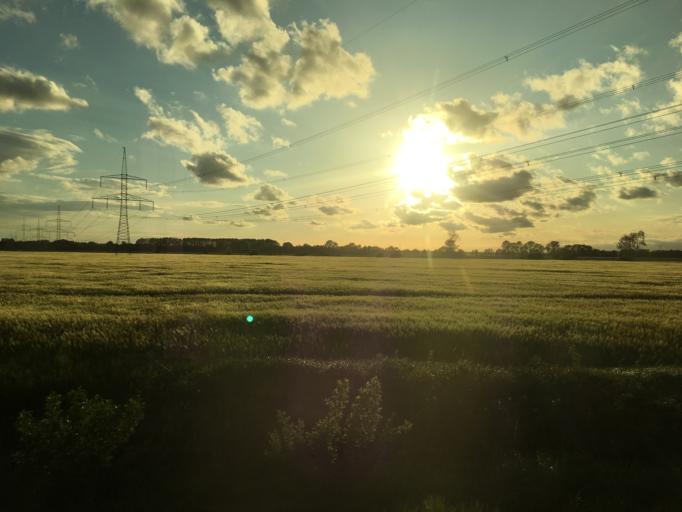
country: DE
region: Brandenburg
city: Doberlug-Kirchhain
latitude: 51.6483
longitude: 13.5781
